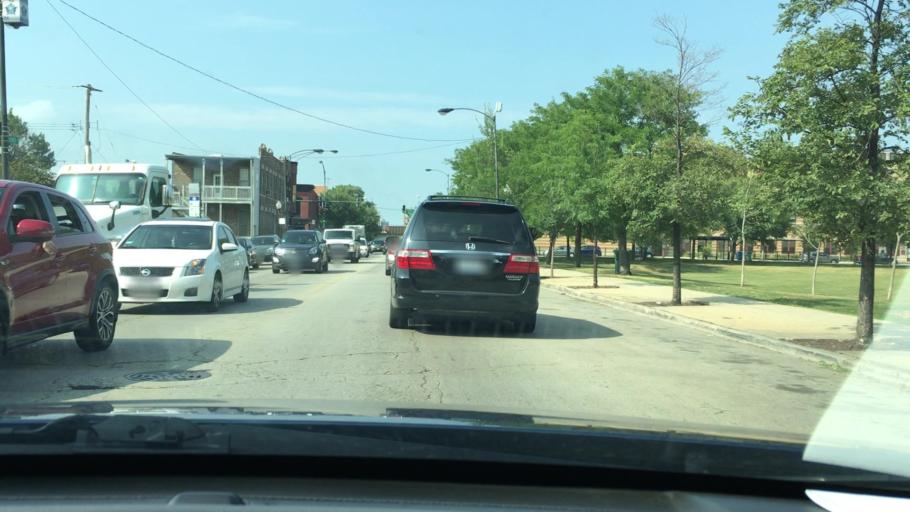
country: US
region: Illinois
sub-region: Cook County
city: Chicago
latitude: 41.8567
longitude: -87.6759
